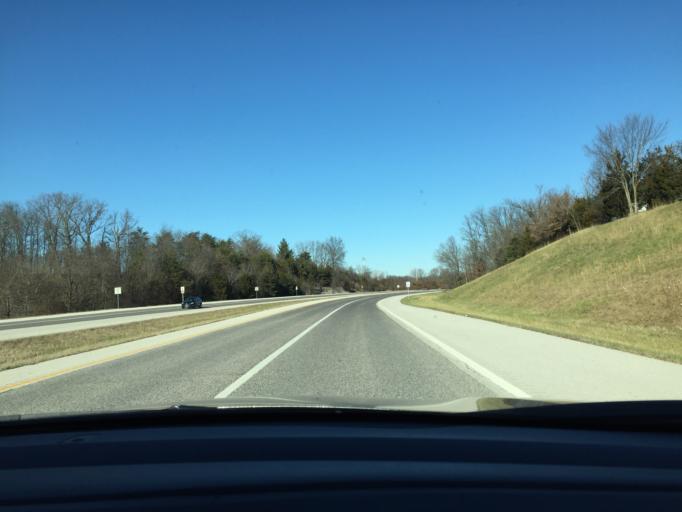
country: US
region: Missouri
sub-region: Saint Louis County
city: Wildwood
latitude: 38.5792
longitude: -90.6856
